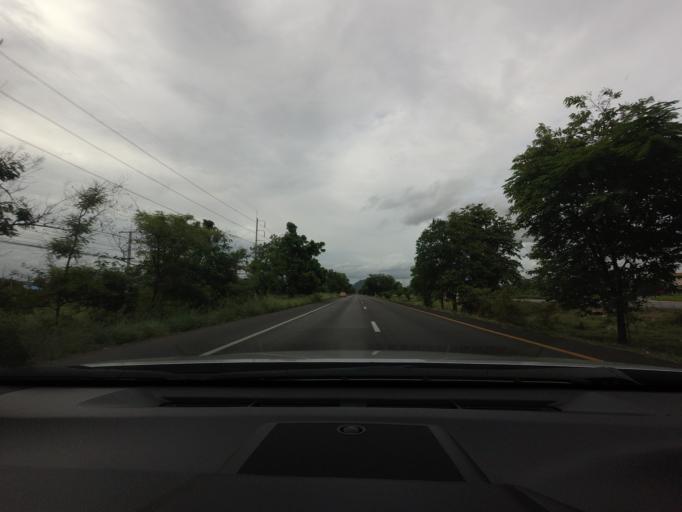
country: TH
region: Prachuap Khiri Khan
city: Hua Hin
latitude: 12.6653
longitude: 99.8773
